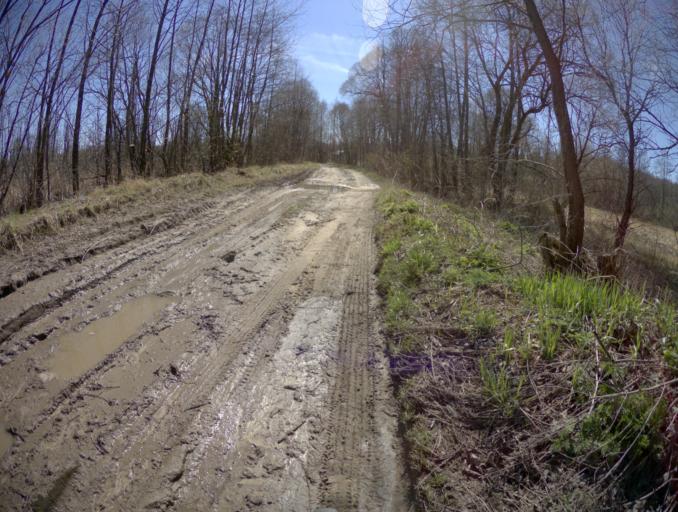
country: RU
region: Vladimir
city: Ivanishchi
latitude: 55.8553
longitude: 40.4457
